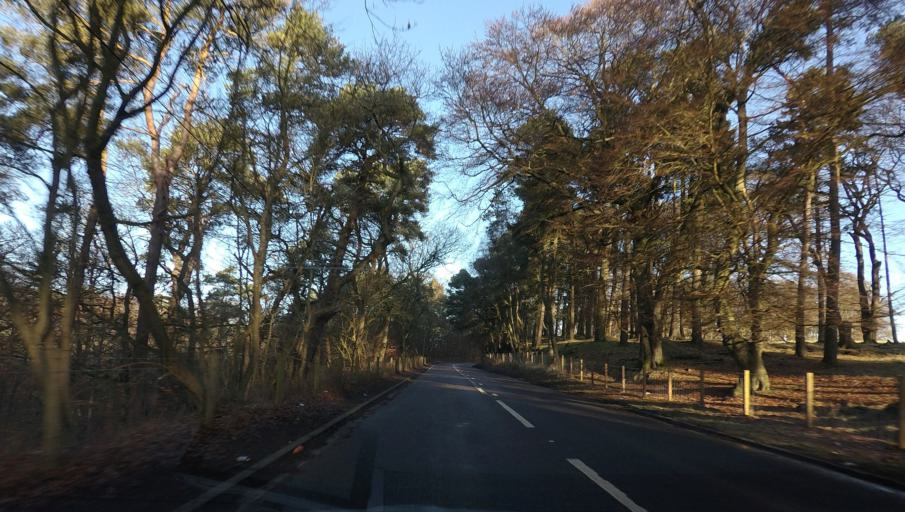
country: GB
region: Scotland
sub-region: North Lanarkshire
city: Newmains
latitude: 55.8000
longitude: -3.8498
